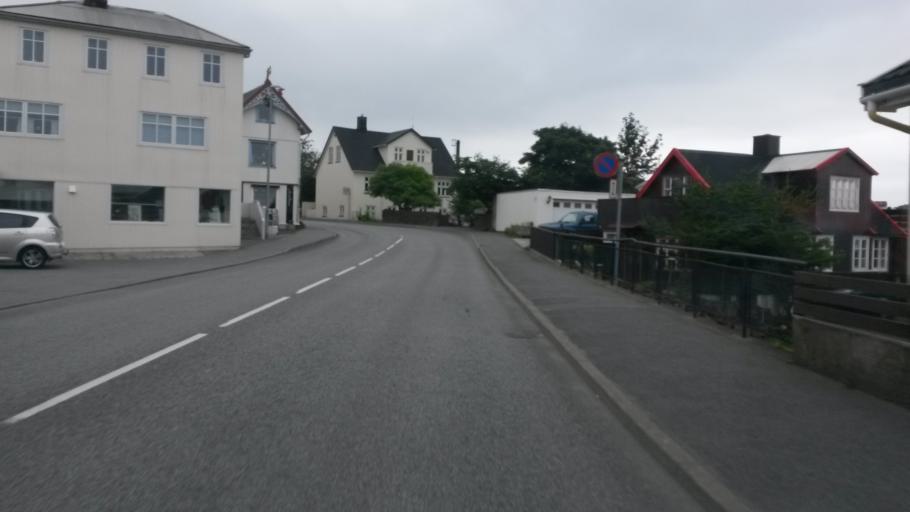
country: FO
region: Streymoy
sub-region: Torshavn
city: Torshavn
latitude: 62.0077
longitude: -6.7778
